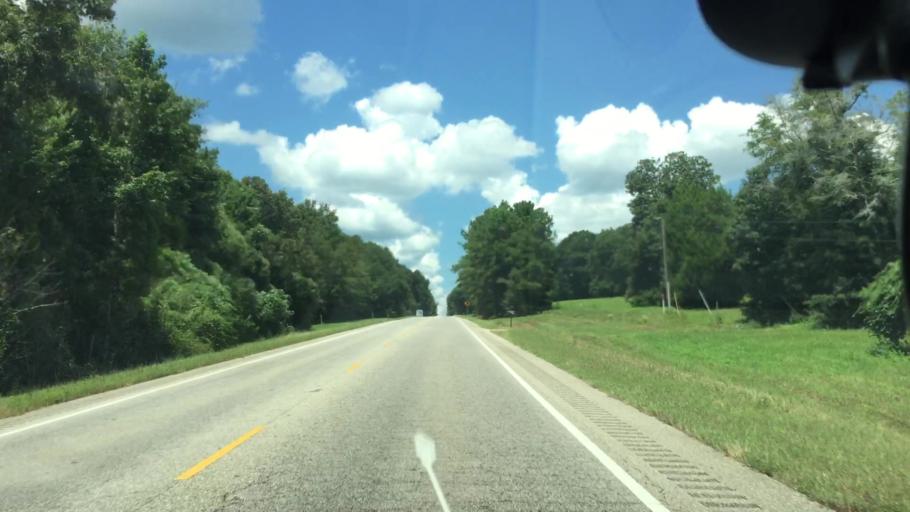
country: US
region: Alabama
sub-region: Coffee County
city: New Brockton
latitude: 31.4457
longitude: -85.8940
